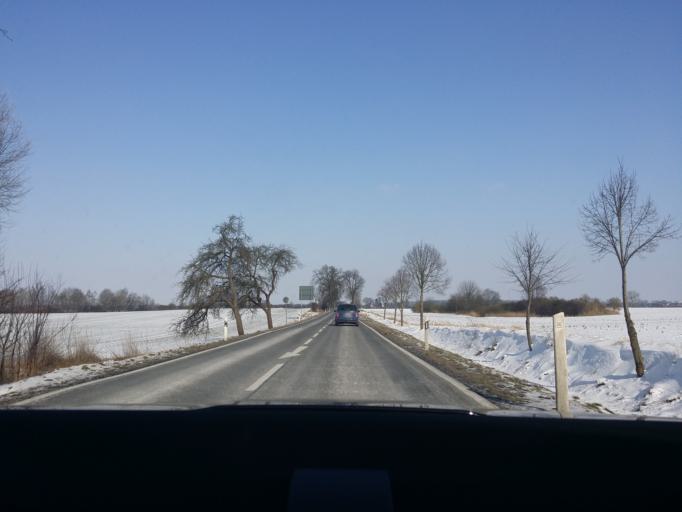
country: DE
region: Mecklenburg-Vorpommern
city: Wulkenzin
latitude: 53.5336
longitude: 13.1441
